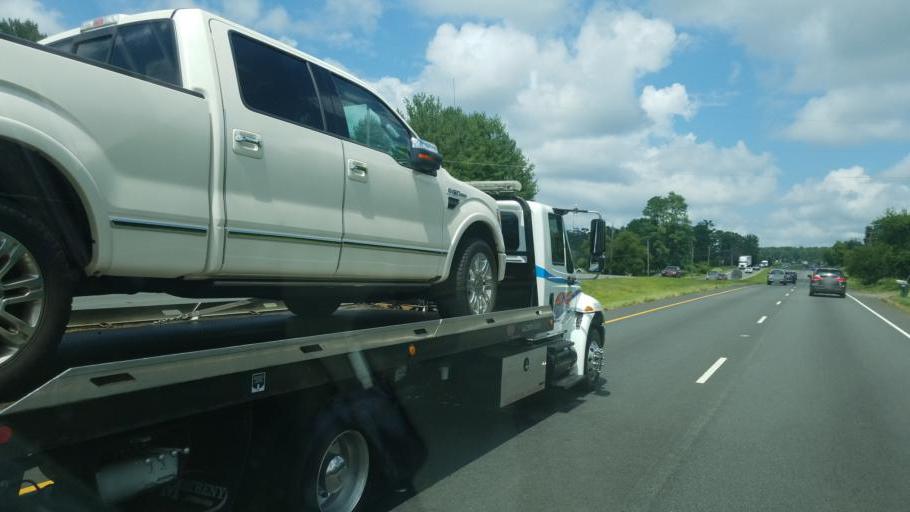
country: US
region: Virginia
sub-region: Fauquier County
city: Warrenton
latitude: 38.6656
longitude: -77.7954
